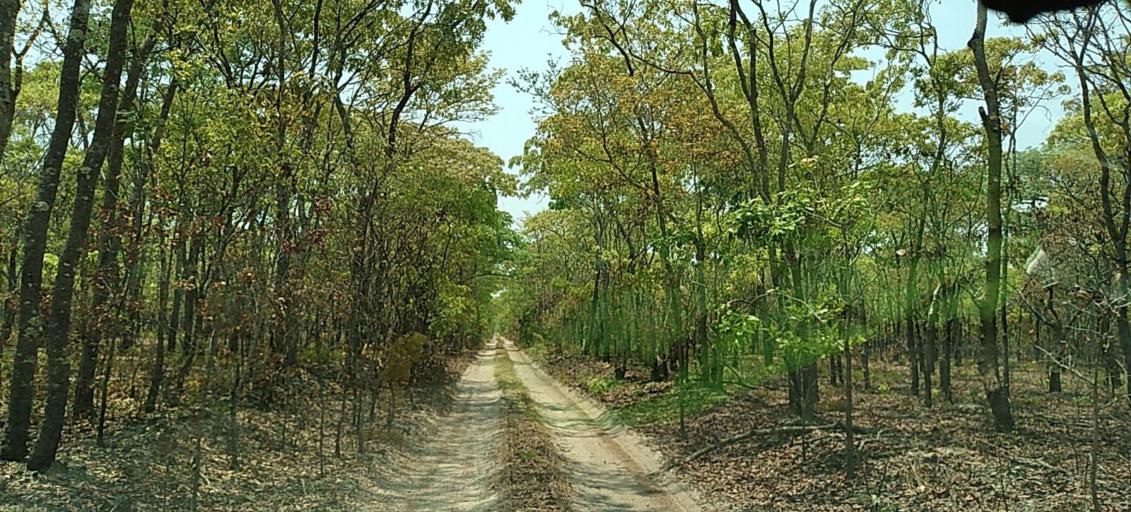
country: ZM
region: North-Western
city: Kabompo
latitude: -13.6537
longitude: 24.4686
